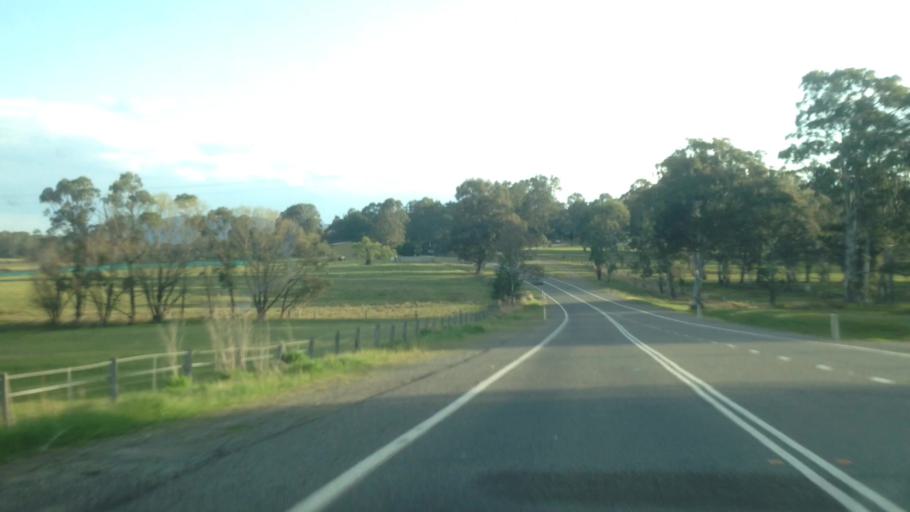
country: AU
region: New South Wales
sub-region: Cessnock
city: Kurri Kurri
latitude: -32.8631
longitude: 151.4816
